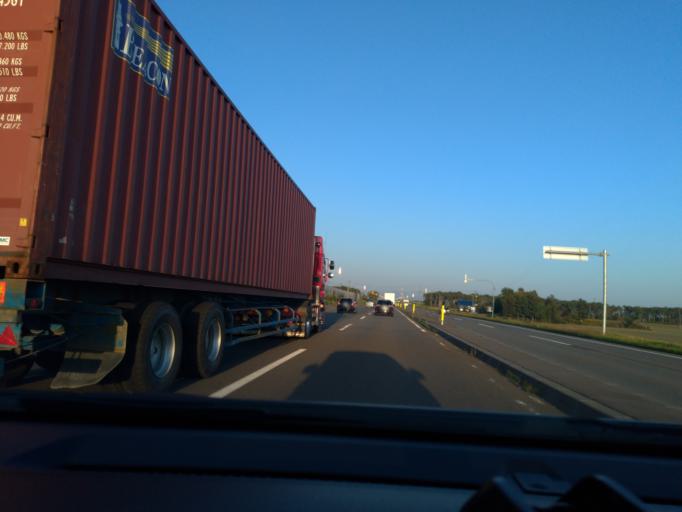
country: JP
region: Hokkaido
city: Tobetsu
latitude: 43.1801
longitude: 141.4738
